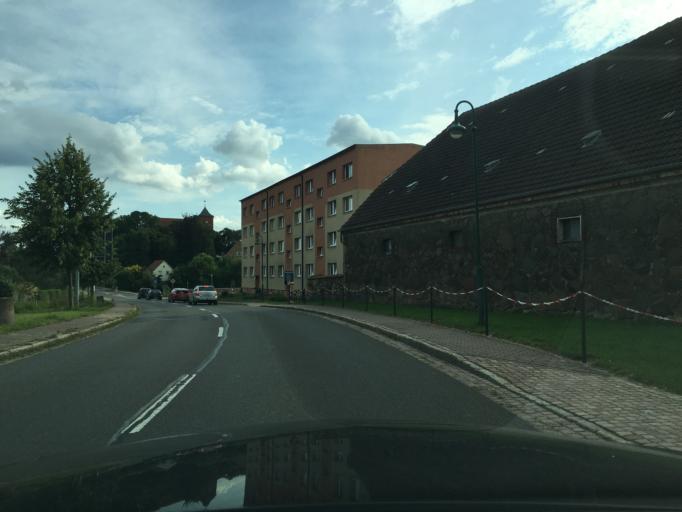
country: DE
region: Mecklenburg-Vorpommern
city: Penzlin
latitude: 53.4492
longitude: 13.0525
